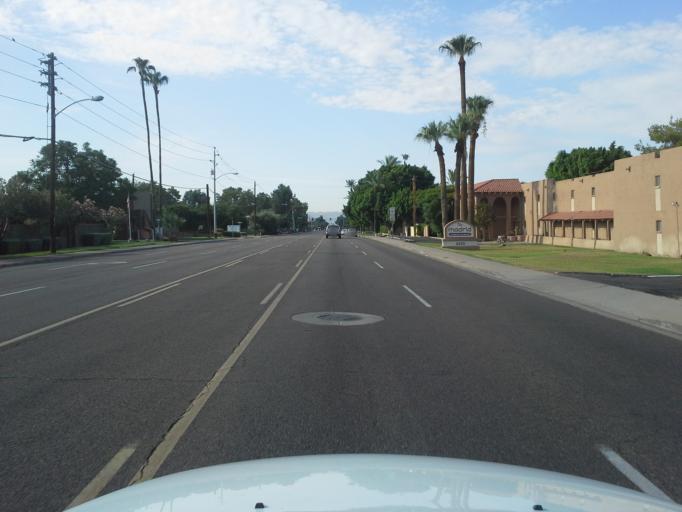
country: US
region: Arizona
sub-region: Maricopa County
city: Phoenix
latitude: 33.5302
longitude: -112.0476
